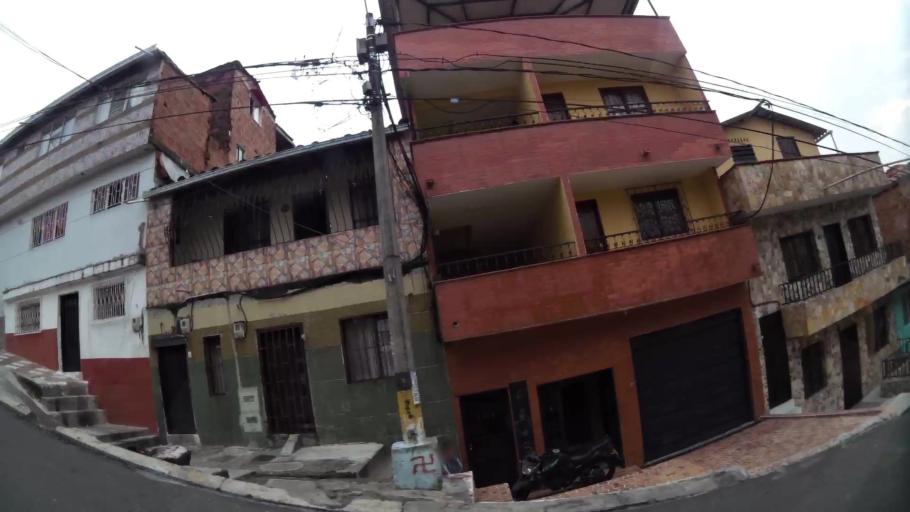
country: CO
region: Antioquia
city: Medellin
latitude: 6.2757
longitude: -75.5601
